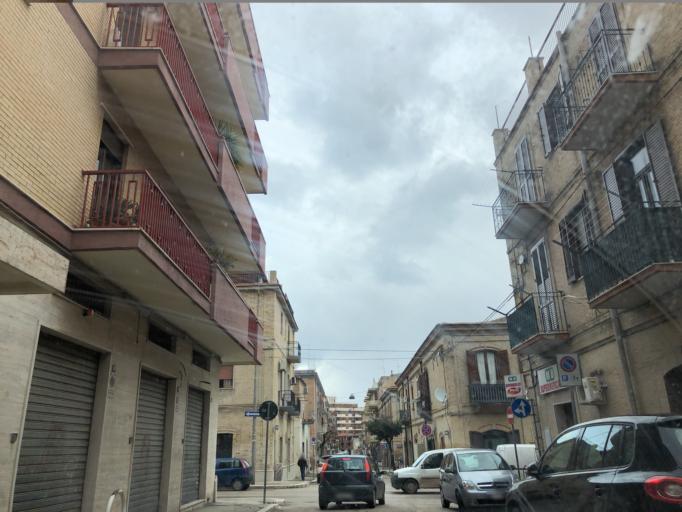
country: IT
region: Apulia
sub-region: Provincia di Foggia
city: Lucera
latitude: 41.5066
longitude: 15.3299
